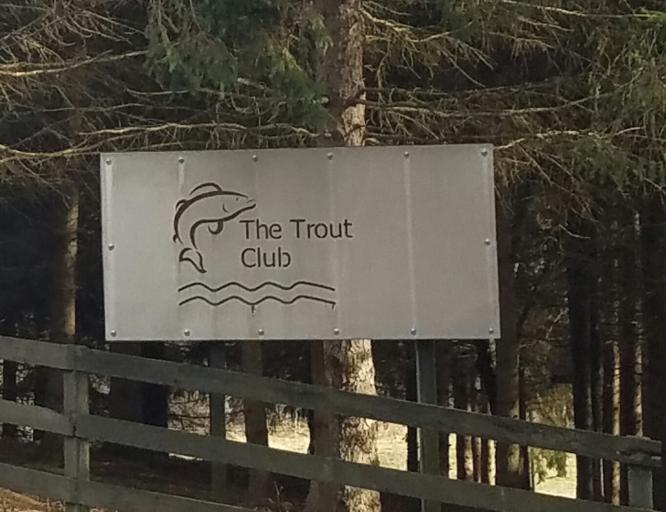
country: US
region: Ohio
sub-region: Knox County
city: Oak Hill
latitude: 40.4361
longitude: -82.1184
